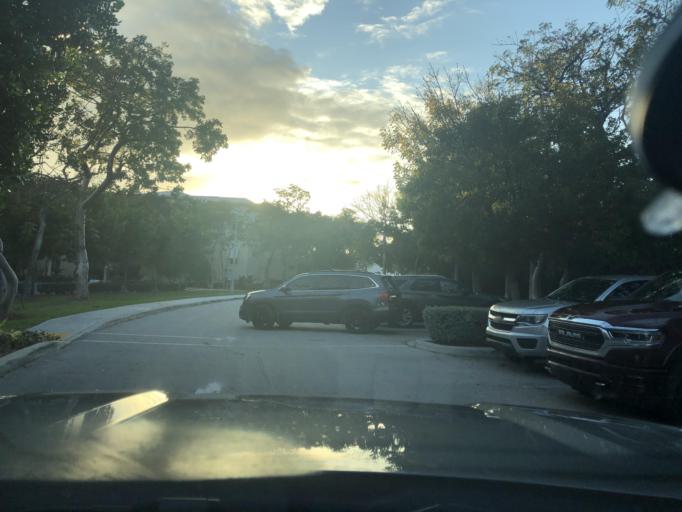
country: US
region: Florida
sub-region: Monroe County
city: Key Largo
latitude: 25.0746
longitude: -80.4637
